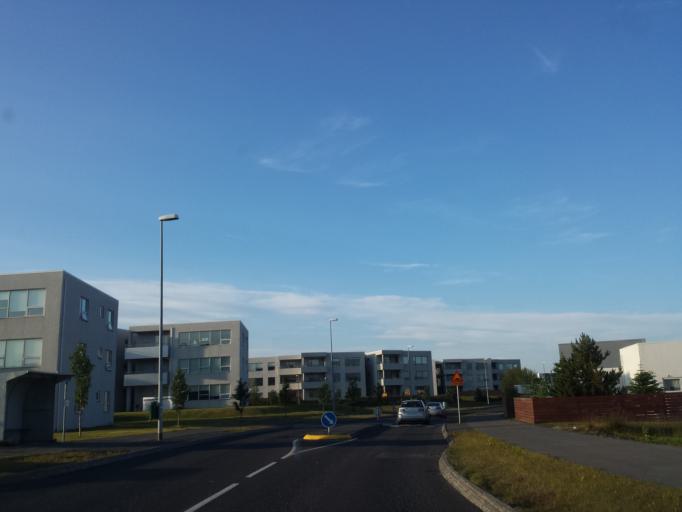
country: IS
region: Capital Region
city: Mosfellsbaer
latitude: 64.0980
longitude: -21.7770
